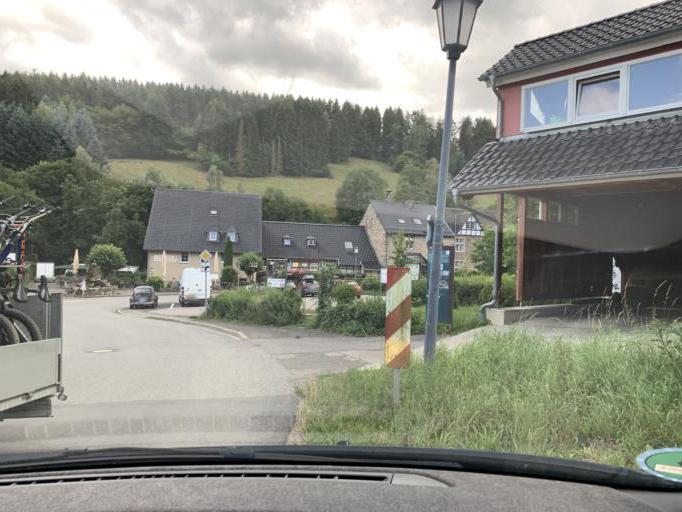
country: DE
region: North Rhine-Westphalia
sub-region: Regierungsbezirk Koln
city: Hurtgenwald
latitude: 50.6672
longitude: 6.3530
